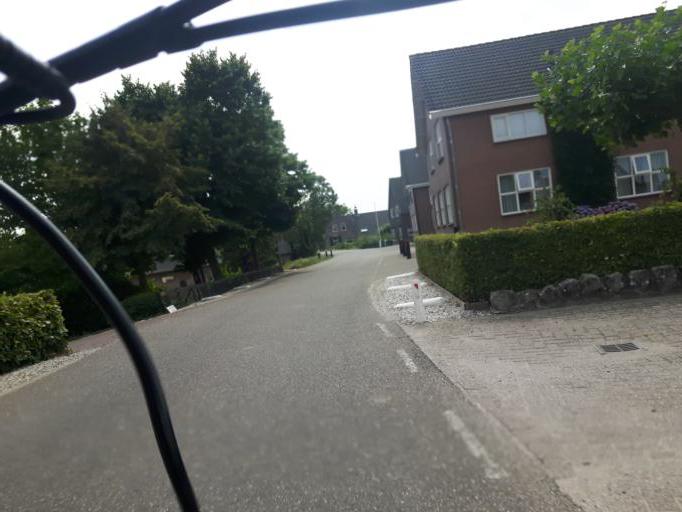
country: NL
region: North Brabant
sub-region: Gemeente Aalburg
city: Aalburg
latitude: 51.8110
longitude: 5.1344
